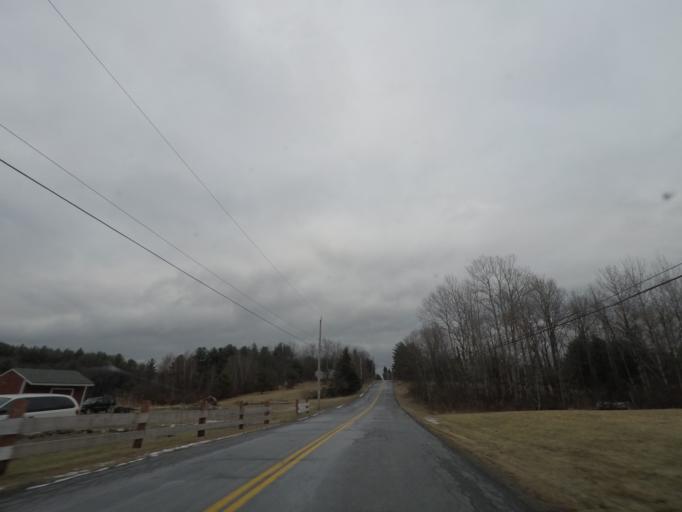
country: US
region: New York
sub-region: Rensselaer County
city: Poestenkill
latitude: 42.7665
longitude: -73.4799
